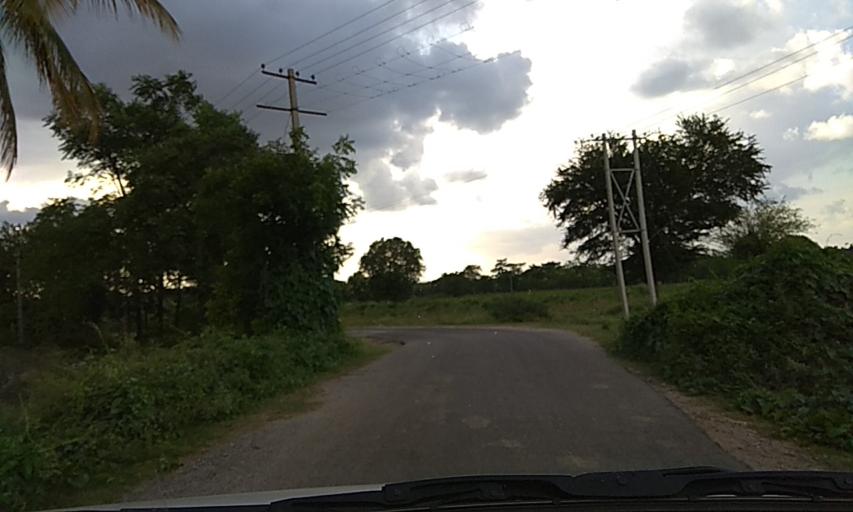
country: IN
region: Karnataka
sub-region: Chamrajnagar
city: Gundlupet
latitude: 11.8716
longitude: 76.7312
